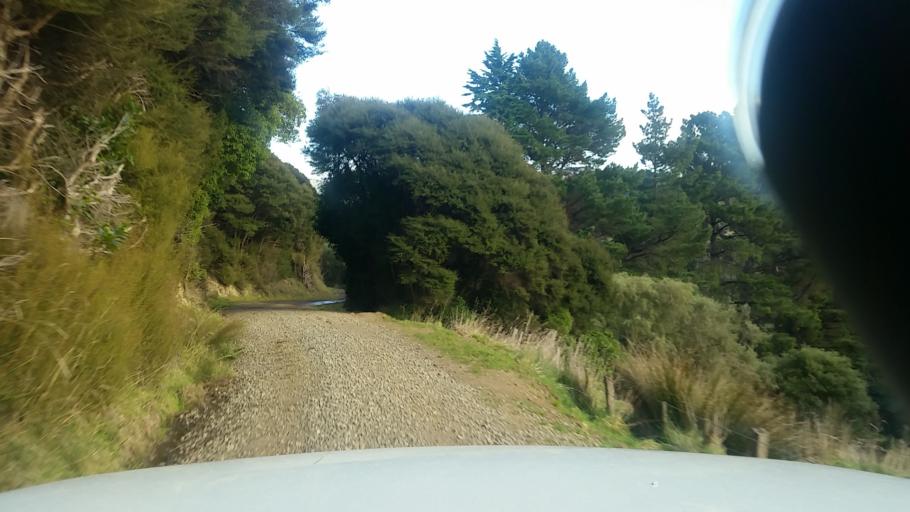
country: NZ
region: Canterbury
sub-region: Christchurch City
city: Christchurch
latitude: -43.7607
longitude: 172.9876
